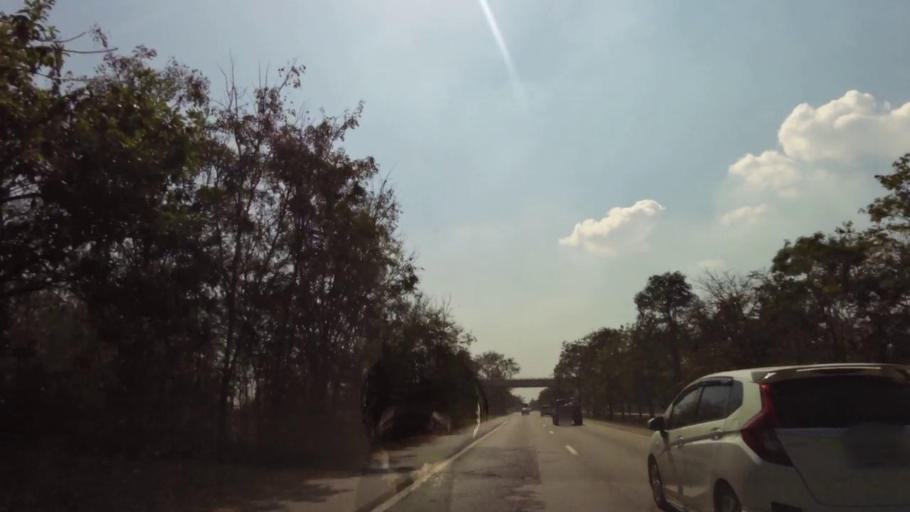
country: TH
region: Phichit
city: Wachira Barami
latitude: 16.5513
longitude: 100.1467
